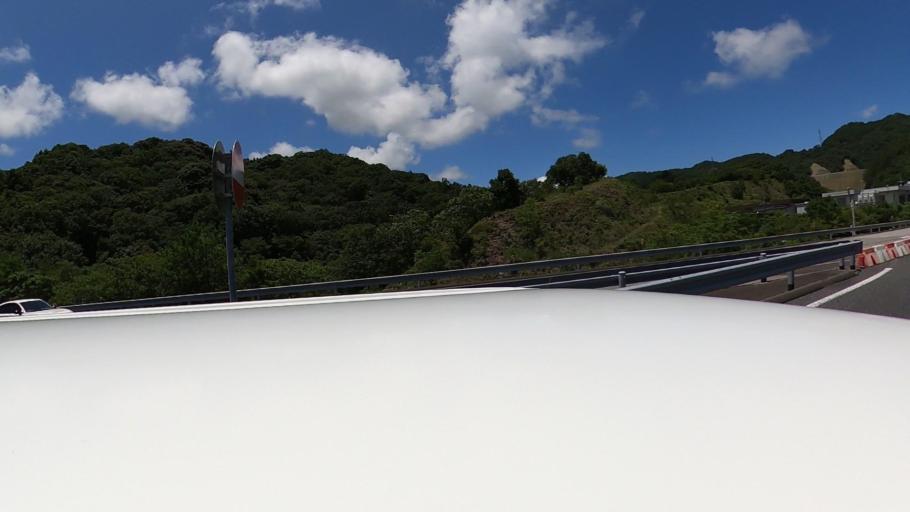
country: JP
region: Miyazaki
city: Nobeoka
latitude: 32.5022
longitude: 131.6619
